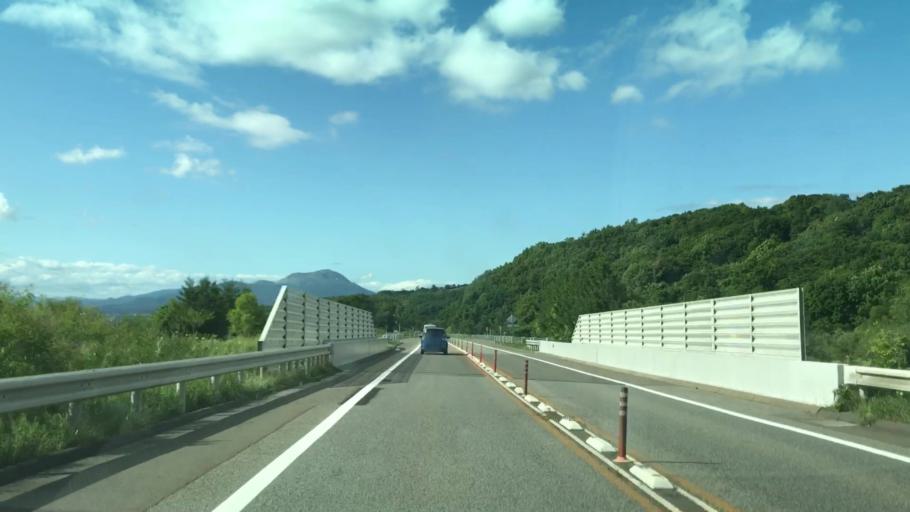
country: JP
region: Hokkaido
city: Date
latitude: 42.4275
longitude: 140.9268
